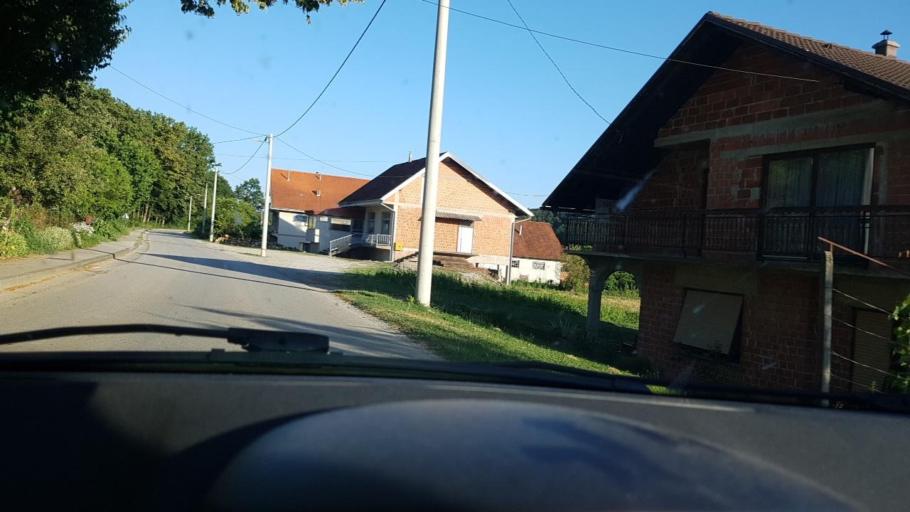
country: HR
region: Krapinsko-Zagorska
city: Bedekovcina
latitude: 46.0773
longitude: 15.9863
